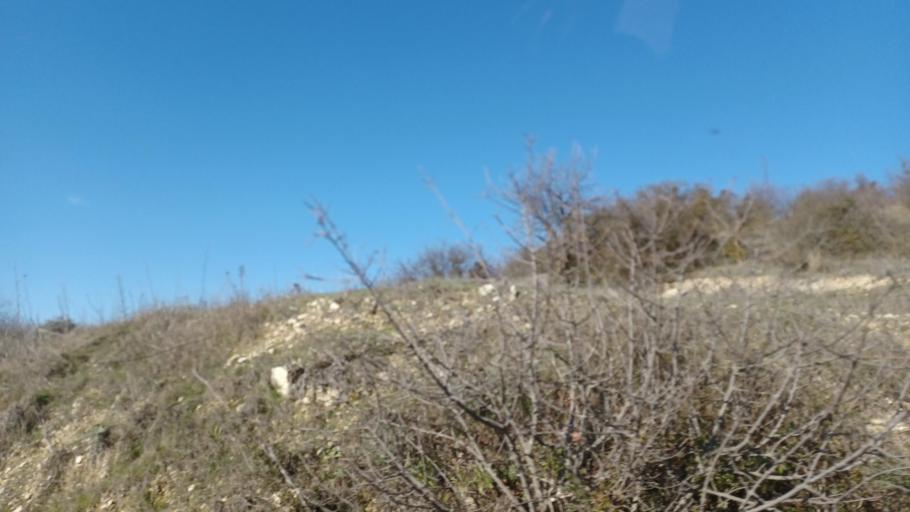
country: CY
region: Limassol
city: Pachna
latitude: 34.8109
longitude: 32.6685
